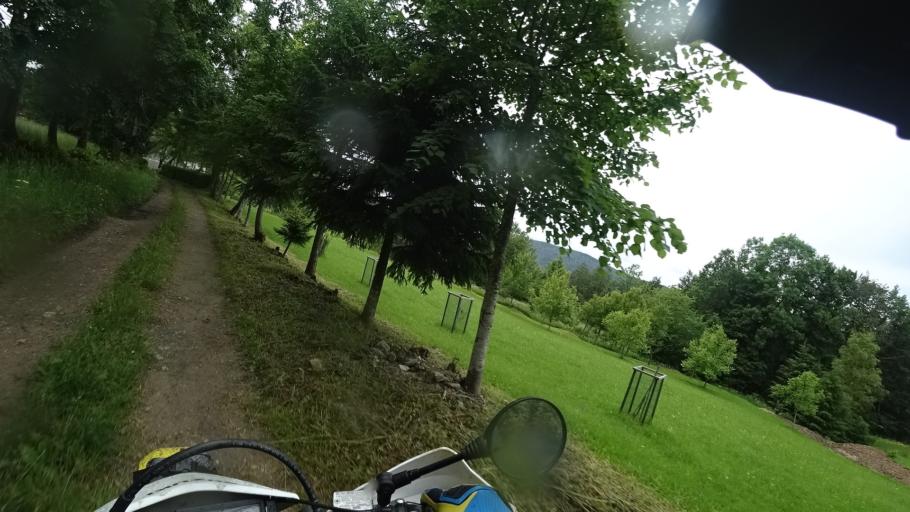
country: HR
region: Primorsko-Goranska
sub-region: Grad Delnice
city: Delnice
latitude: 45.3773
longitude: 14.8990
